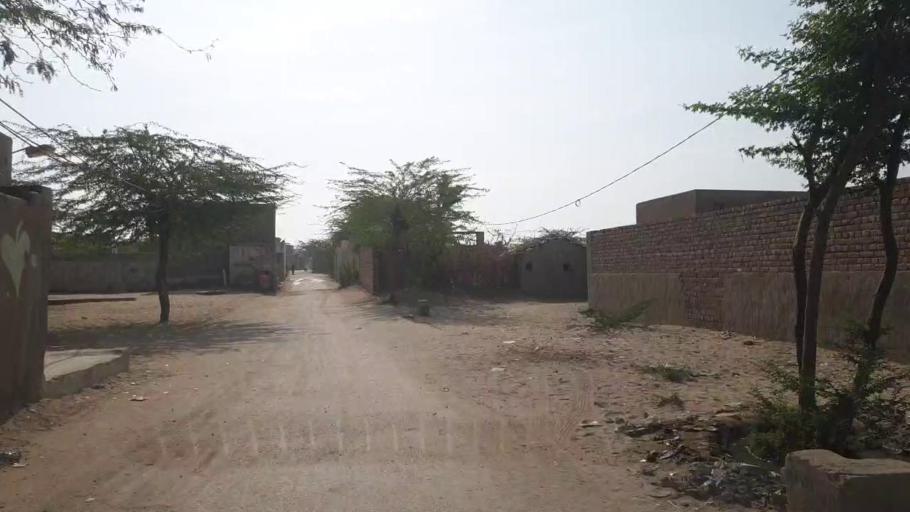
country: PK
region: Sindh
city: Umarkot
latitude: 25.3410
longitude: 69.7400
